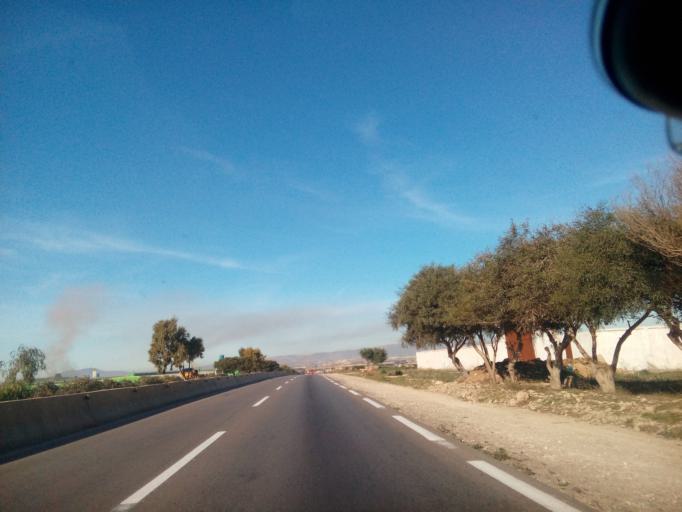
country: DZ
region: Oran
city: Ain el Bya
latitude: 35.7727
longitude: -0.2462
